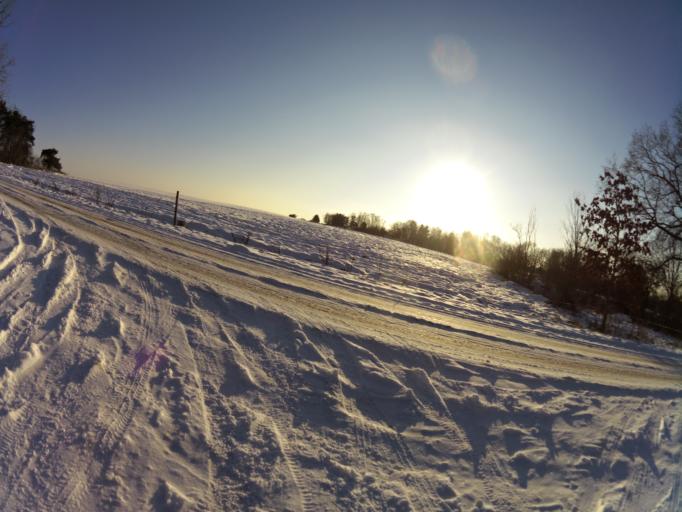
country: PL
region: West Pomeranian Voivodeship
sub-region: Powiat stargardzki
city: Dobrzany
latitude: 53.3335
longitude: 15.3979
